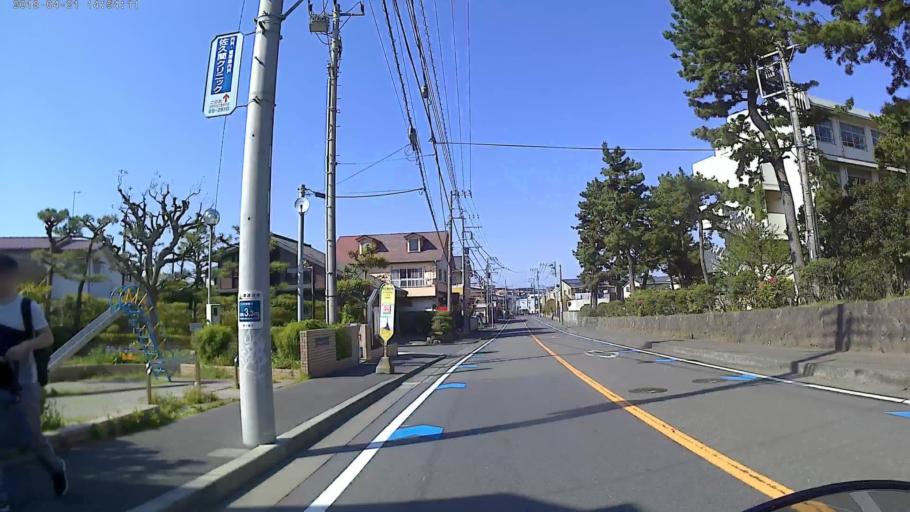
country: JP
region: Kanagawa
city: Chigasaki
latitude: 35.3188
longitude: 139.3868
